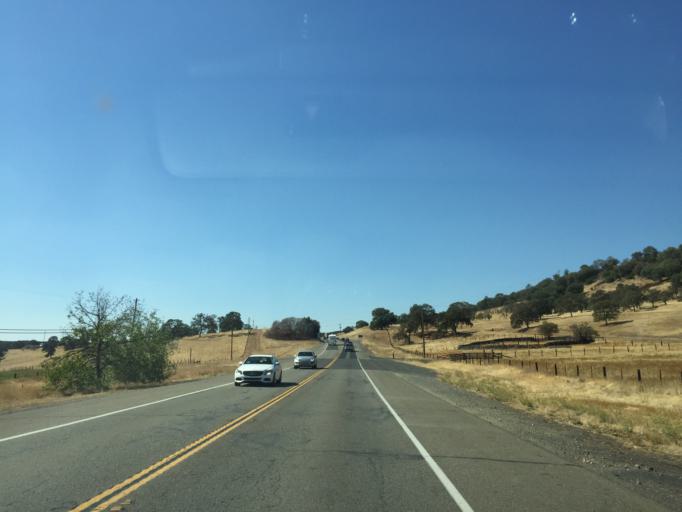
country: US
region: California
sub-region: Tuolumne County
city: Jamestown
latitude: 37.9047
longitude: -120.4729
